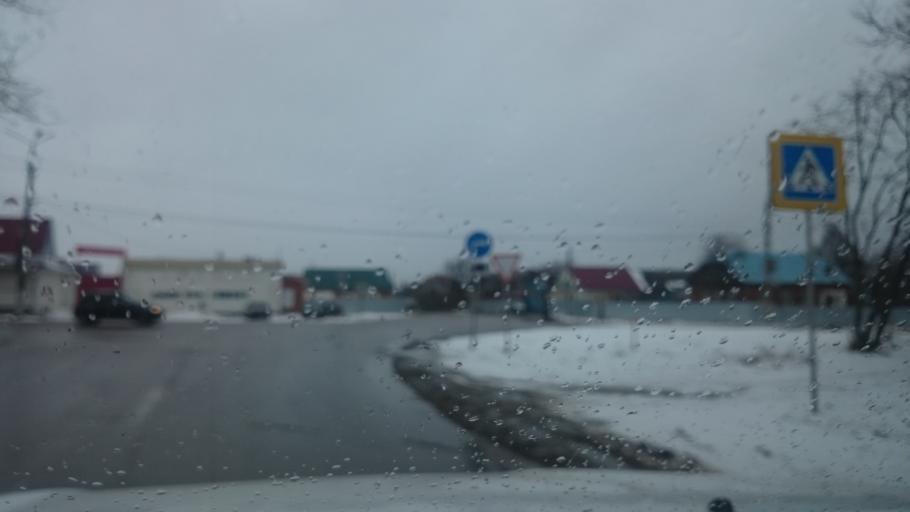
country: RU
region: Tula
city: Mendeleyevskiy
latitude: 54.1973
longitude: 37.5424
